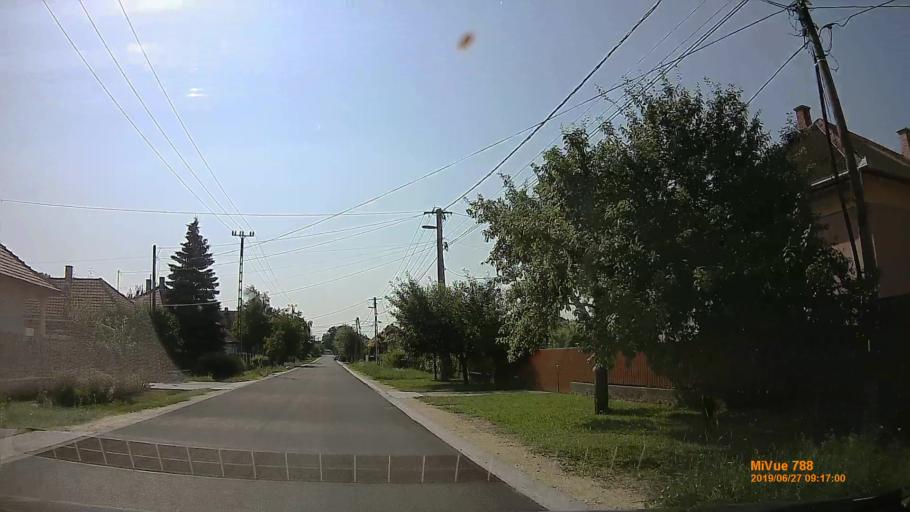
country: HU
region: Pest
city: Ullo
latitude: 47.3942
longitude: 19.3596
